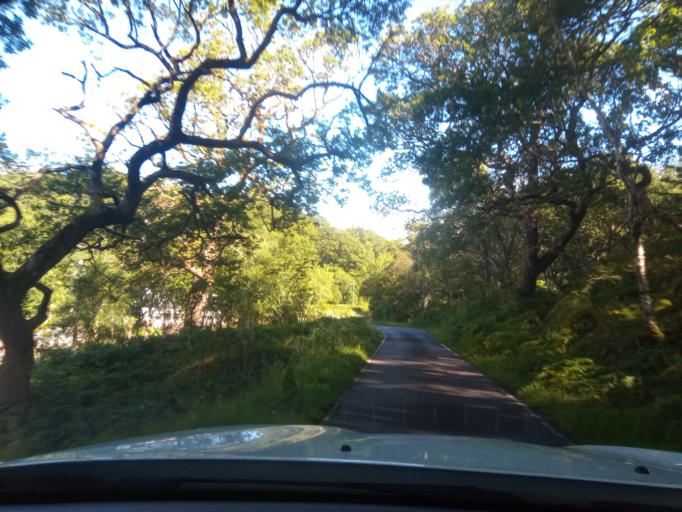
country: GB
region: Scotland
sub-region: Argyll and Bute
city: Isle Of Mull
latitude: 56.6894
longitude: -5.6683
